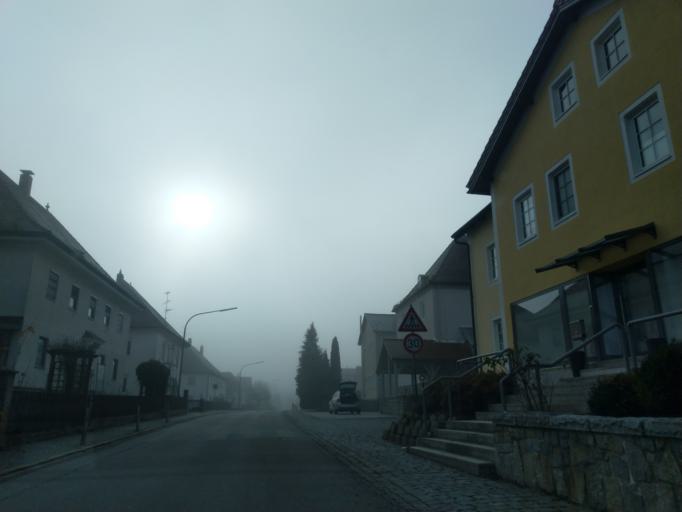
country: DE
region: Bavaria
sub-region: Lower Bavaria
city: Schollnach
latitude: 48.7539
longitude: 13.1794
